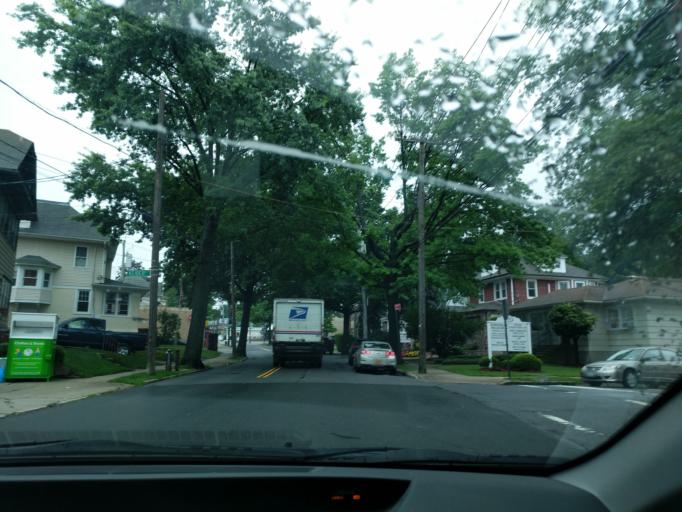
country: US
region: New Jersey
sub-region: Hudson County
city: Bayonne
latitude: 40.6186
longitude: -74.1234
